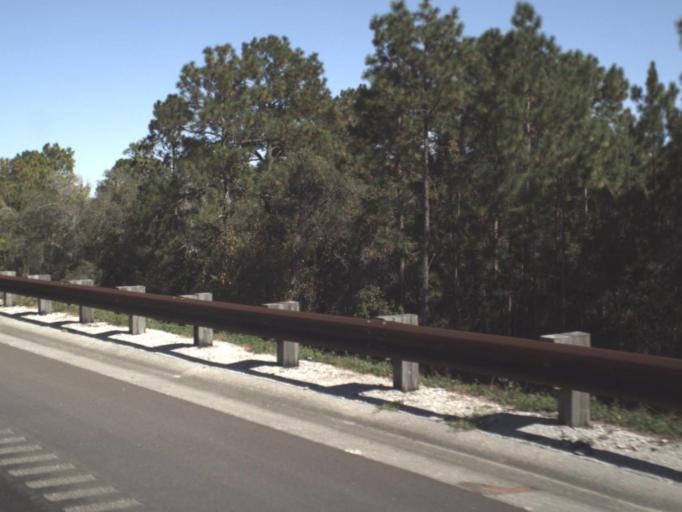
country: US
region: Florida
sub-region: Hernando County
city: Brookridge
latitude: 28.5234
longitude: -82.4786
